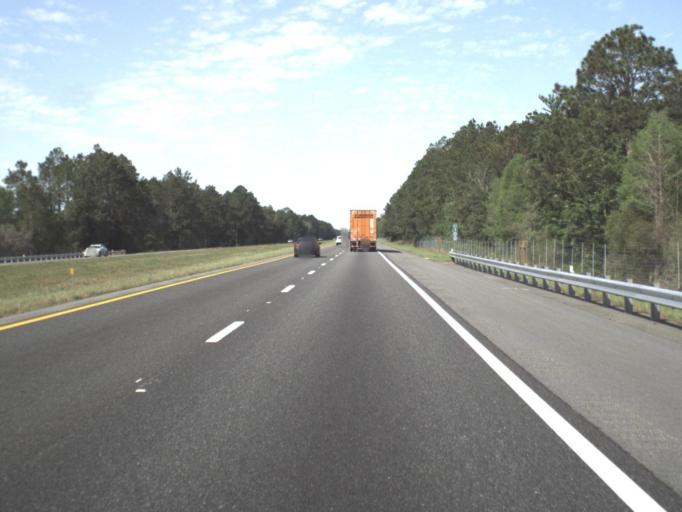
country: US
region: Florida
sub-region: Holmes County
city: Bonifay
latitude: 30.7433
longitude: -85.8741
